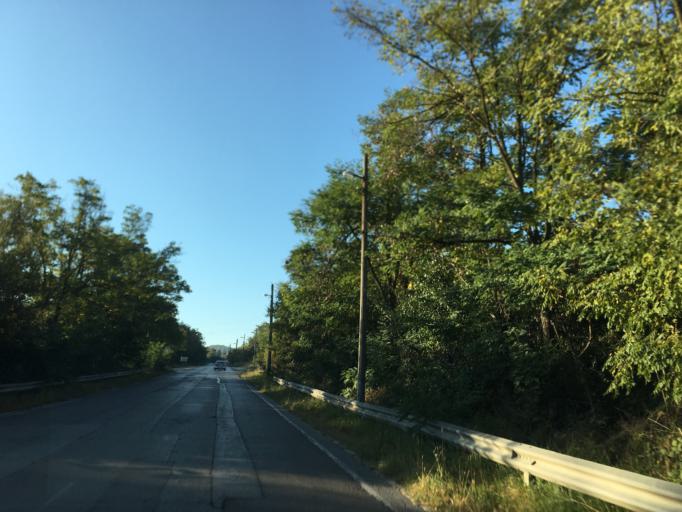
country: BG
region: Sofiya
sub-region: Obshtina Ikhtiman
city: Ikhtiman
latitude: 42.3802
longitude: 23.8763
